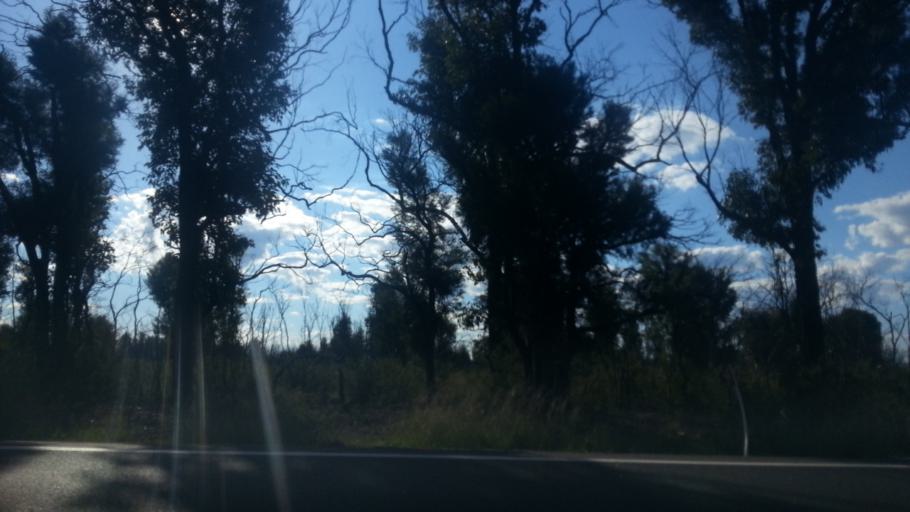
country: AU
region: New South Wales
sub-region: Penrith Municipality
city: Werrington Downs
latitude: -33.7024
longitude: 150.7248
